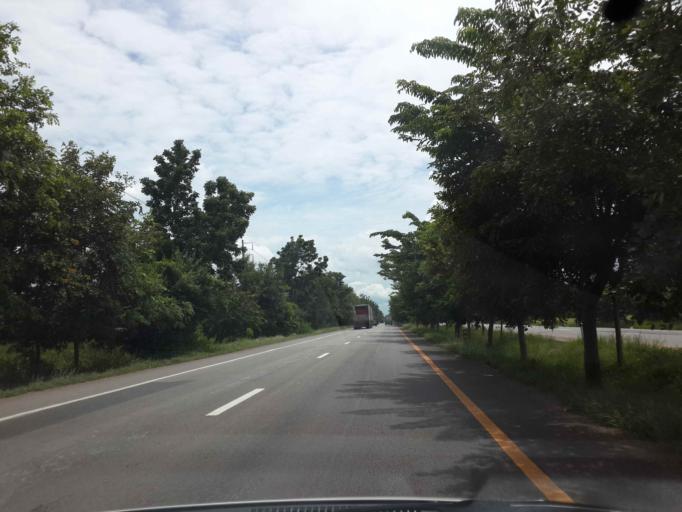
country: TH
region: Ratchaburi
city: Pak Tho
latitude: 13.3990
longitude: 99.8149
